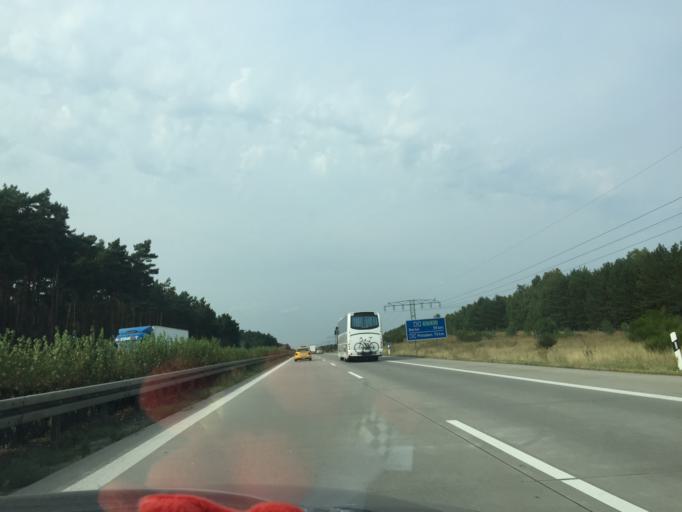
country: DE
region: Brandenburg
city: Schwerin
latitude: 52.1291
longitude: 13.6472
